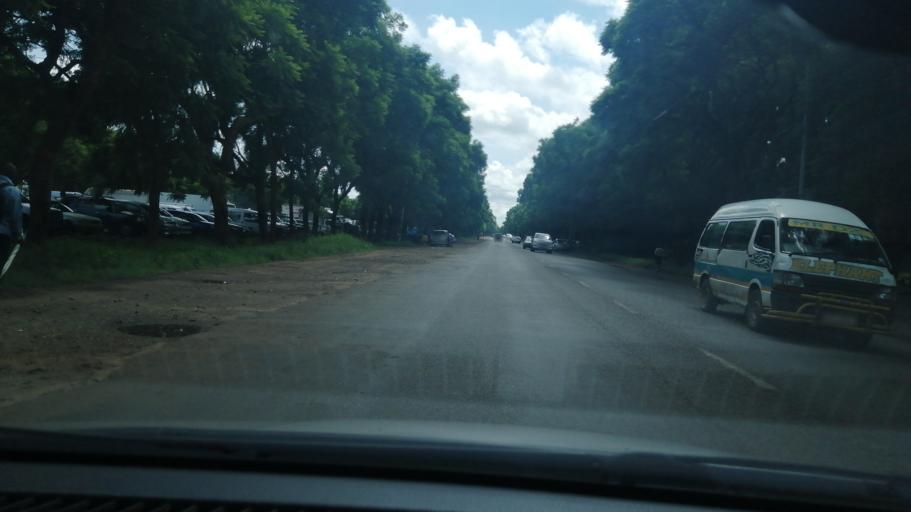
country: ZW
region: Harare
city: Harare
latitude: -17.8193
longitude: 31.0336
